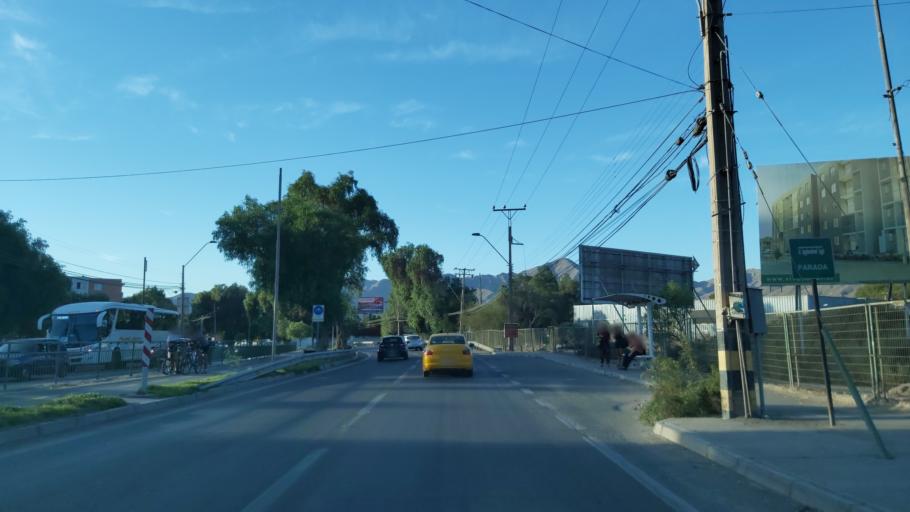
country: CL
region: Atacama
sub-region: Provincia de Copiapo
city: Copiapo
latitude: -27.3863
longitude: -70.3132
